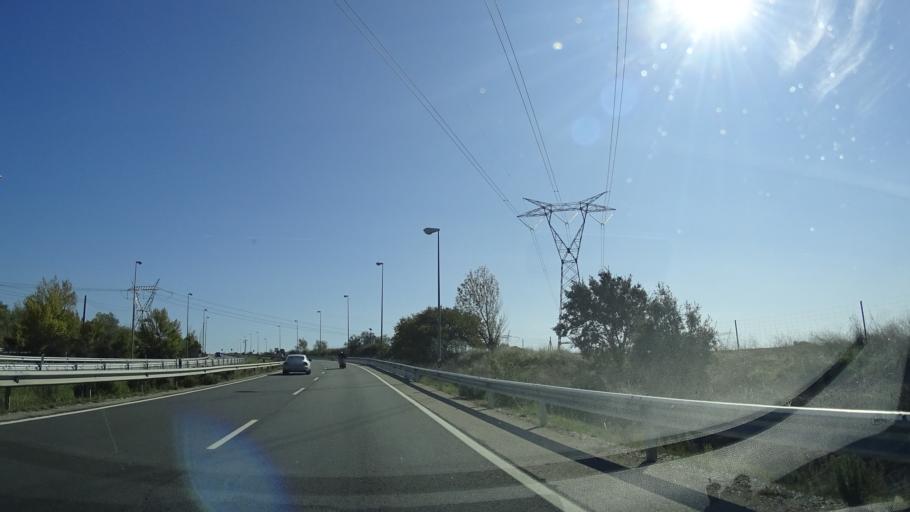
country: ES
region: Madrid
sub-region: Provincia de Madrid
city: Villanueva del Pardillo
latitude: 40.5148
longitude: -3.9326
